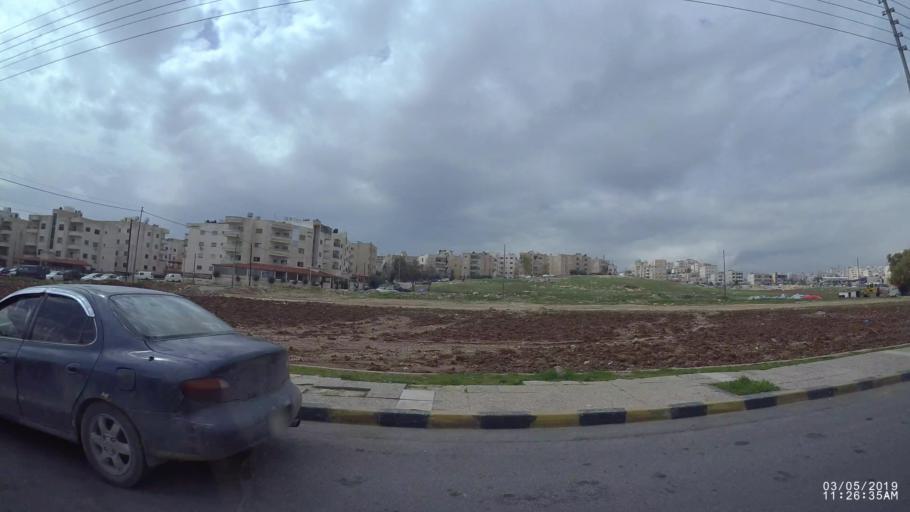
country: JO
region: Amman
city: Amman
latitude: 31.9915
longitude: 35.9297
